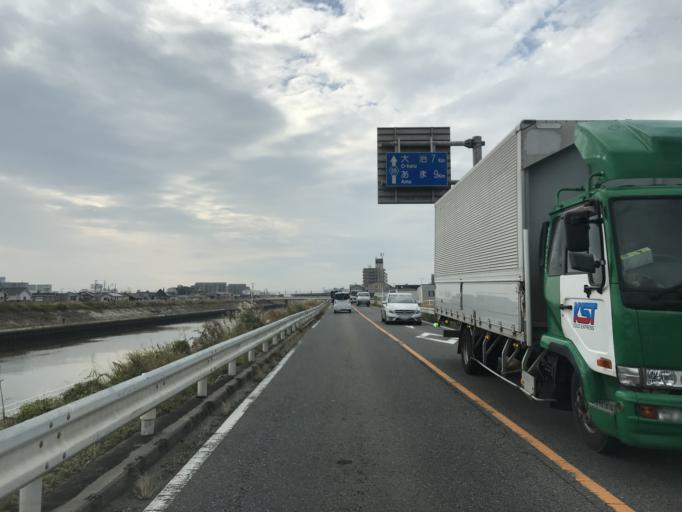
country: JP
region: Aichi
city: Nagoya-shi
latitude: 35.2097
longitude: 136.8611
